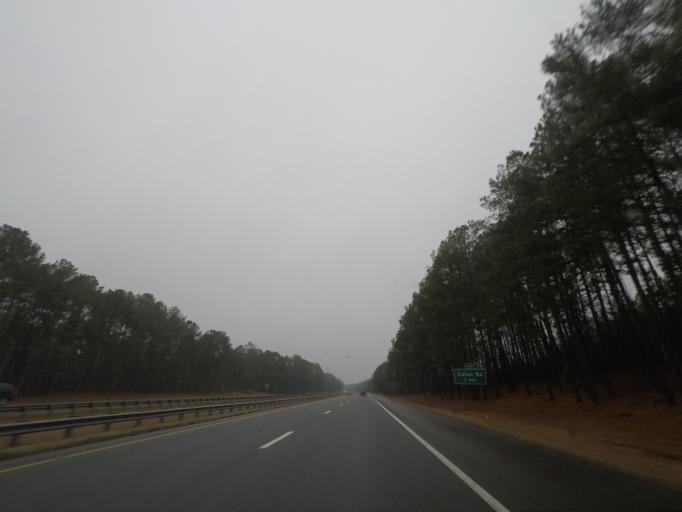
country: US
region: North Carolina
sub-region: Chatham County
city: Farmville
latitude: 35.5745
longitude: -79.1395
